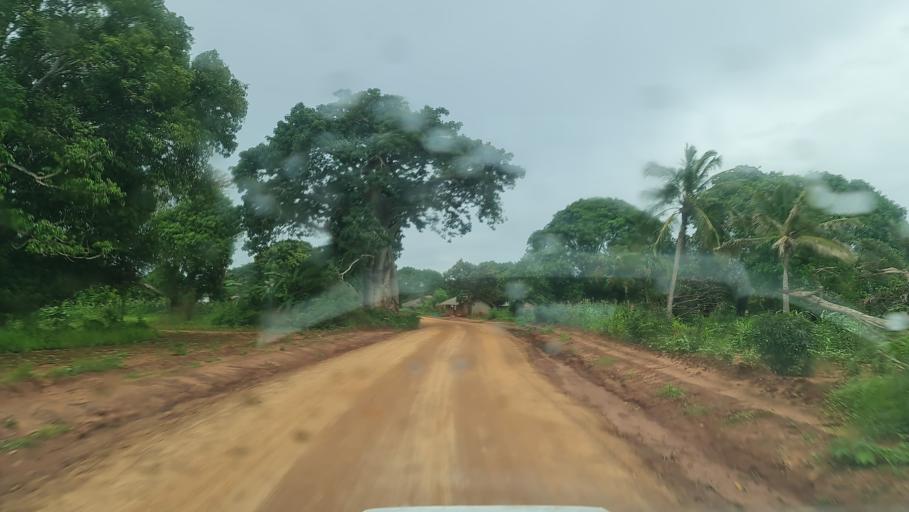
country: MZ
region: Nampula
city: Nacala
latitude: -14.3633
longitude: 40.4788
